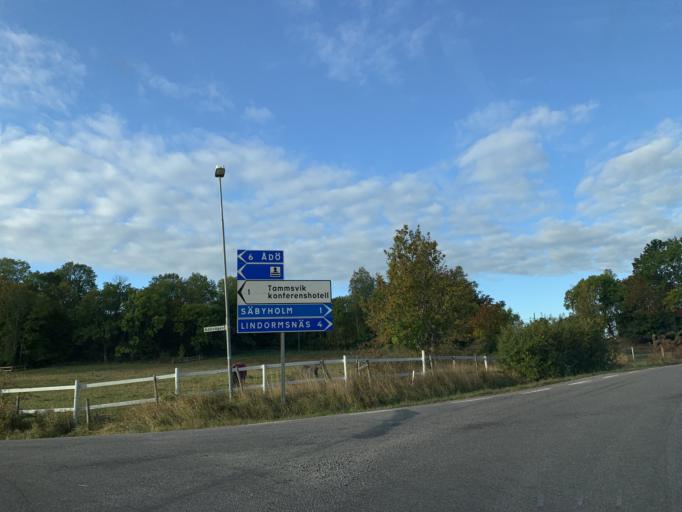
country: SE
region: Stockholm
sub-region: Upplands-Bro Kommun
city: Bro
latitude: 59.5070
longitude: 17.5844
